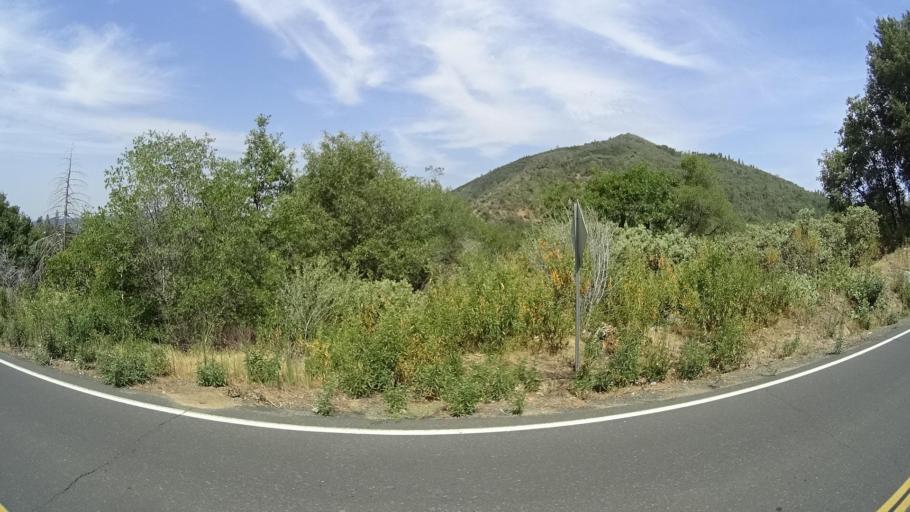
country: US
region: California
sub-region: Mariposa County
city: Midpines
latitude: 37.5107
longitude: -119.8430
